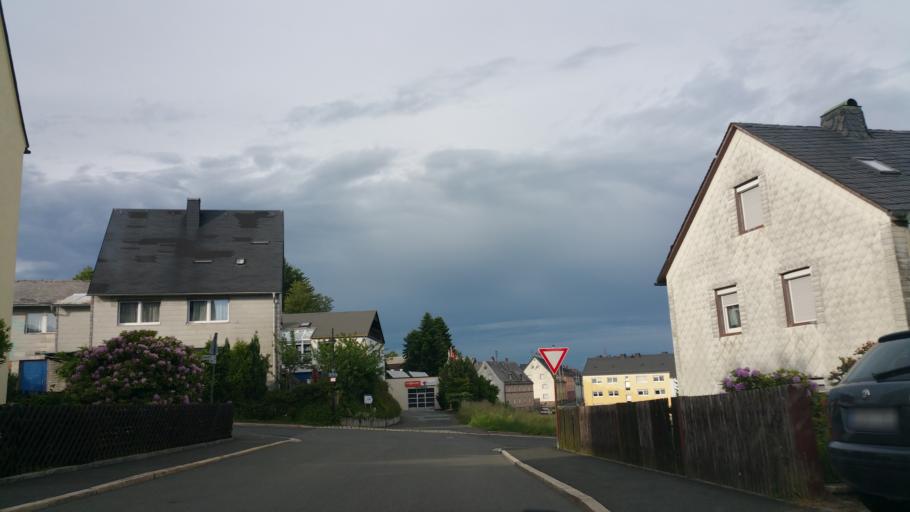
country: DE
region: Bavaria
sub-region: Upper Franconia
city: Helmbrechts
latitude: 50.2323
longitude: 11.7152
